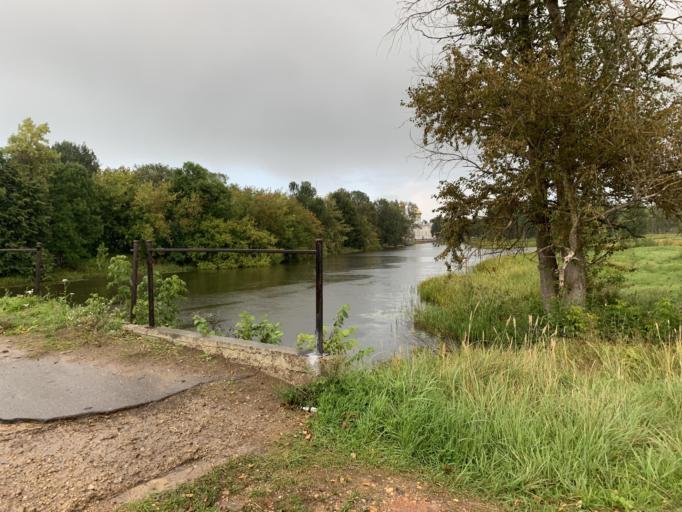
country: RU
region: Tverskaya
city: Vyshniy Volochek
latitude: 57.5809
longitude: 34.5500
